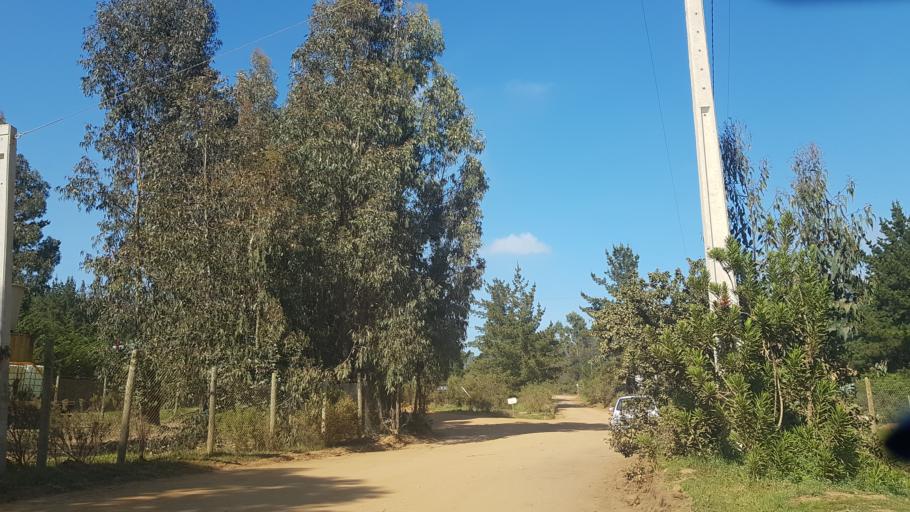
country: CL
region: Valparaiso
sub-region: Provincia de Valparaiso
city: Valparaiso
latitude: -33.1289
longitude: -71.6672
